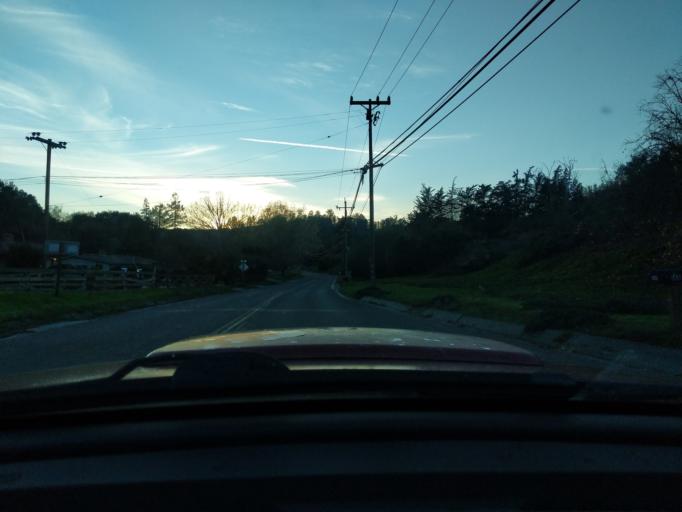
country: US
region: California
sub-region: Monterey County
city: Prunedale
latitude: 36.8247
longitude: -121.6657
